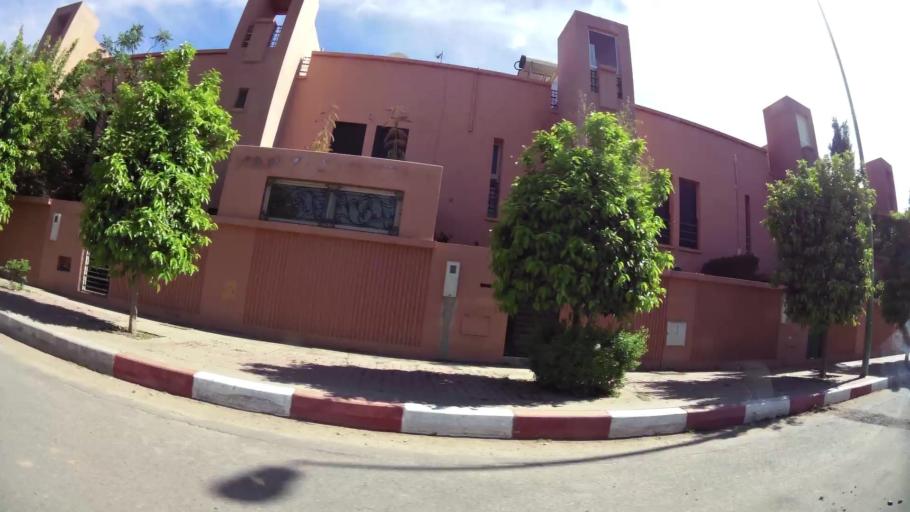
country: MA
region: Marrakech-Tensift-Al Haouz
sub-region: Marrakech
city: Marrakesh
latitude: 31.6586
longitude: -8.0557
